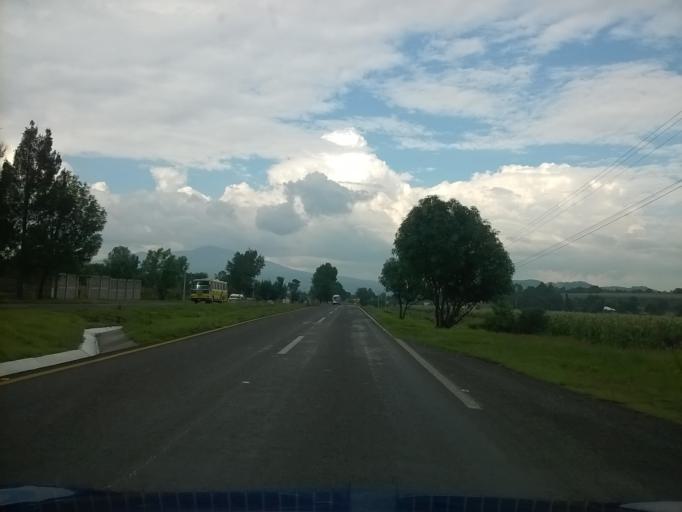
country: MX
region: Michoacan
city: Huiramba
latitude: 19.5383
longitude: -101.4648
